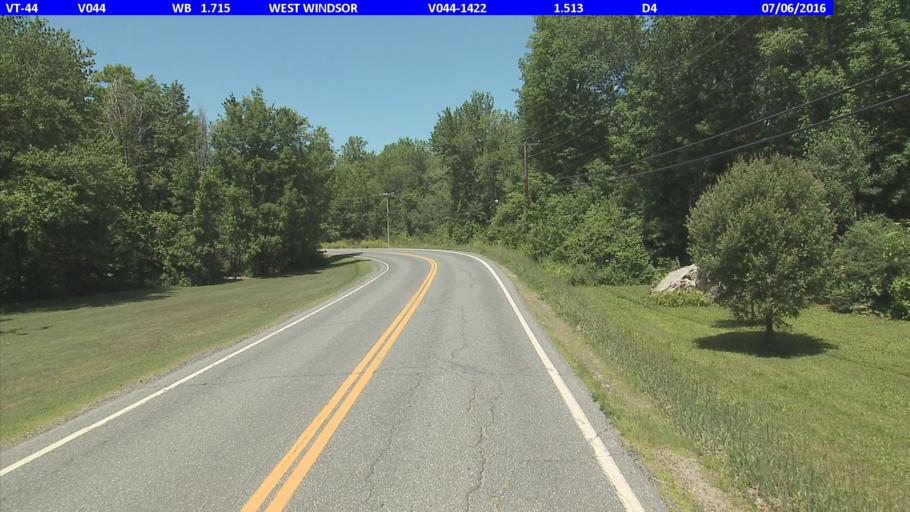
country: US
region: Vermont
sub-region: Windsor County
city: Windsor
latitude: 43.4547
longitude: -72.5126
